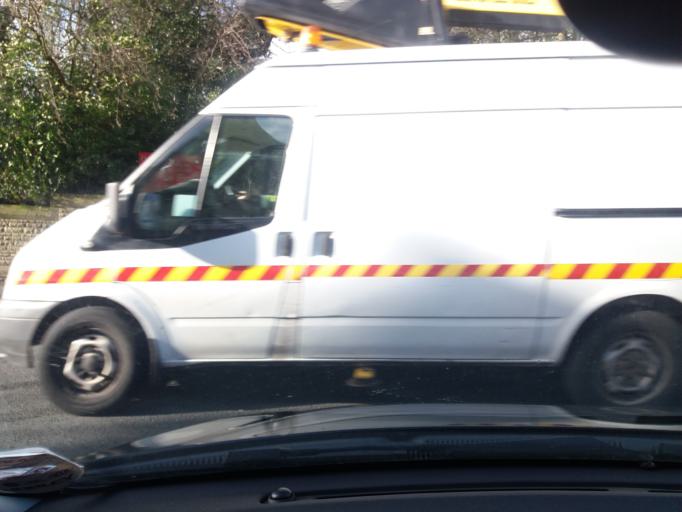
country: GB
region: England
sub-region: Lancashire
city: Adlington
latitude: 53.6157
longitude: -2.5996
